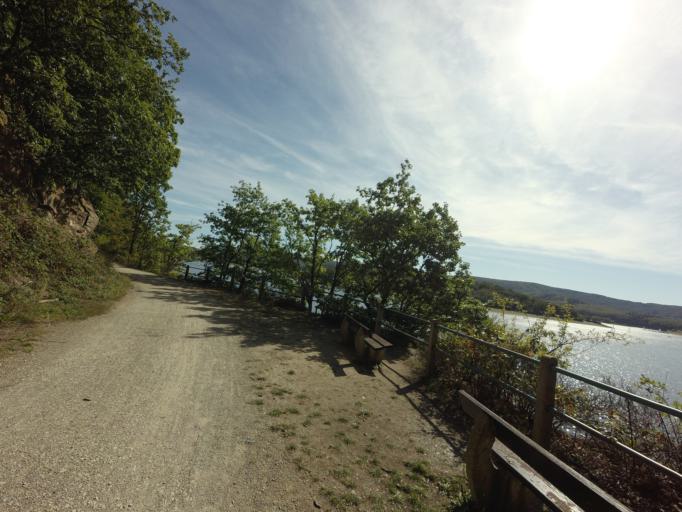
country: DE
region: North Rhine-Westphalia
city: Heimbach
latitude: 50.6497
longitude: 6.4262
